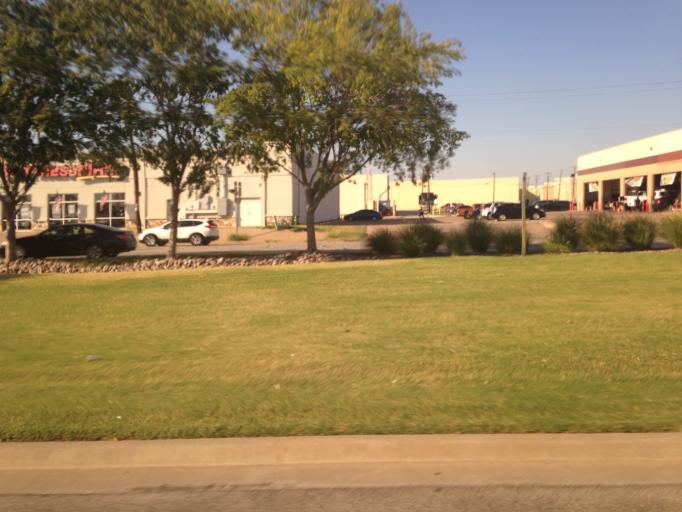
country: US
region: Texas
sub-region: Tarrant County
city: Richland Hills
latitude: 32.8235
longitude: -97.2047
